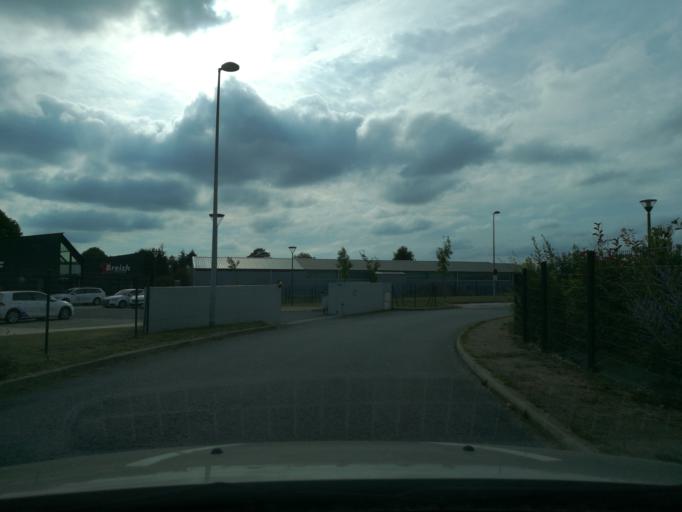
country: FR
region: Brittany
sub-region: Departement d'Ille-et-Vilaine
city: Montauban-de-Bretagne
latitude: 48.1955
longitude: -2.0310
